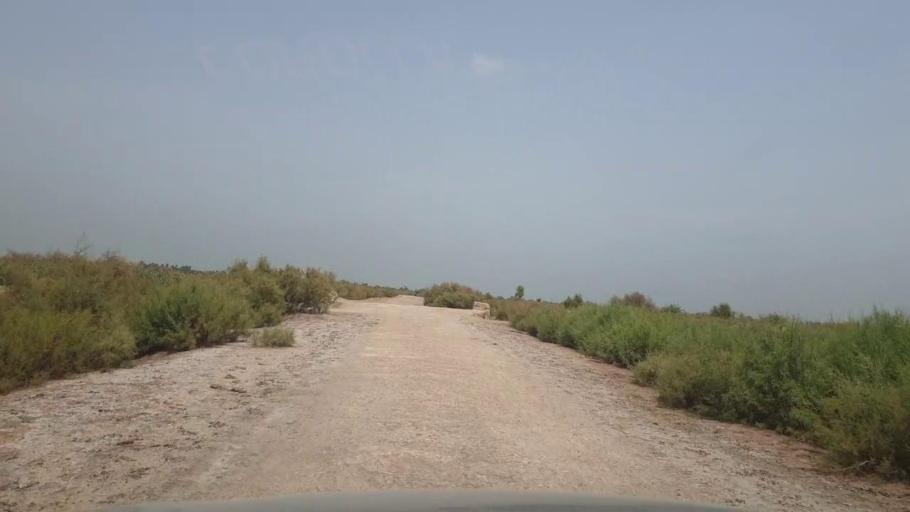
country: PK
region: Sindh
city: Garhi Yasin
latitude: 27.9127
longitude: 68.3800
